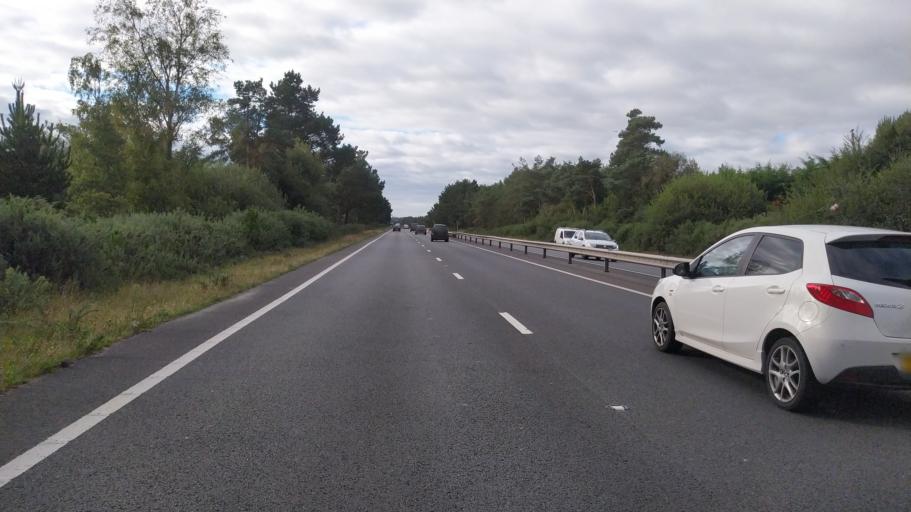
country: GB
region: England
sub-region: Dorset
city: St Leonards
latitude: 50.7963
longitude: -1.8152
